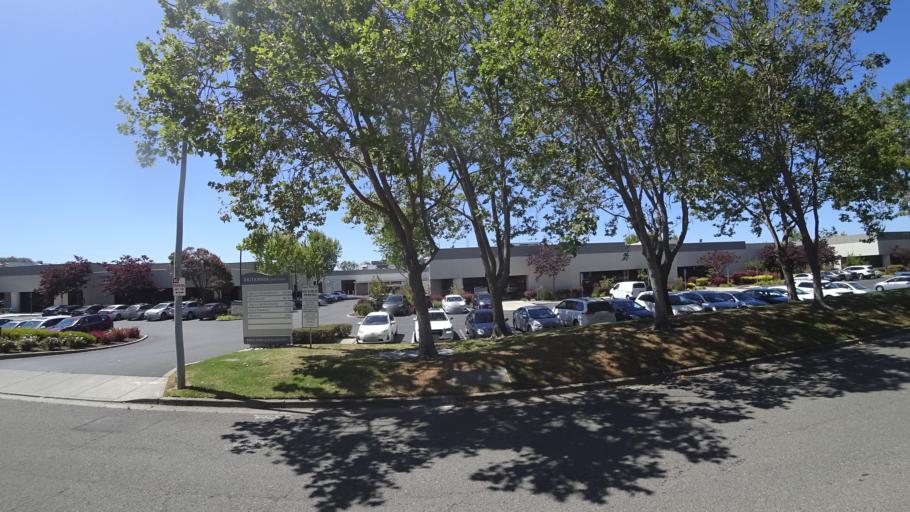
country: US
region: California
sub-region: Alameda County
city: San Lorenzo
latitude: 37.6257
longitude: -122.1241
